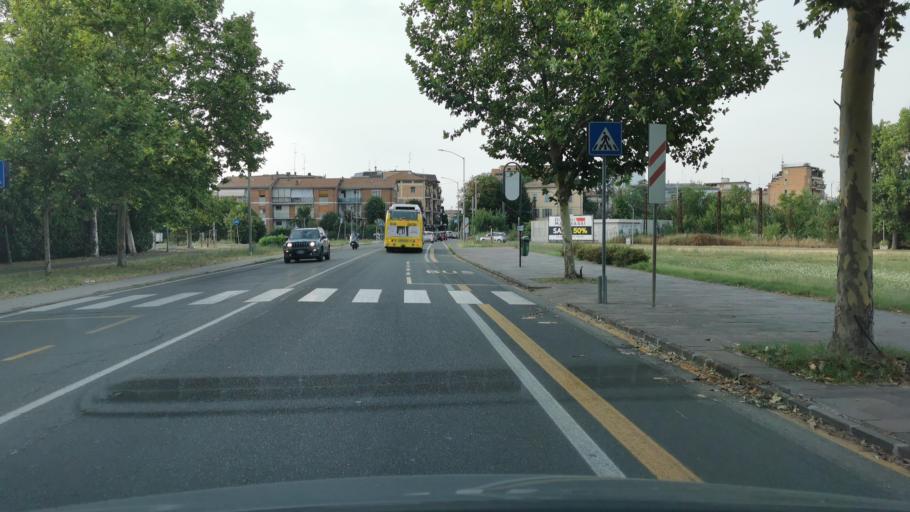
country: IT
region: Emilia-Romagna
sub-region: Provincia di Modena
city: Modena
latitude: 44.6318
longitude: 10.9263
